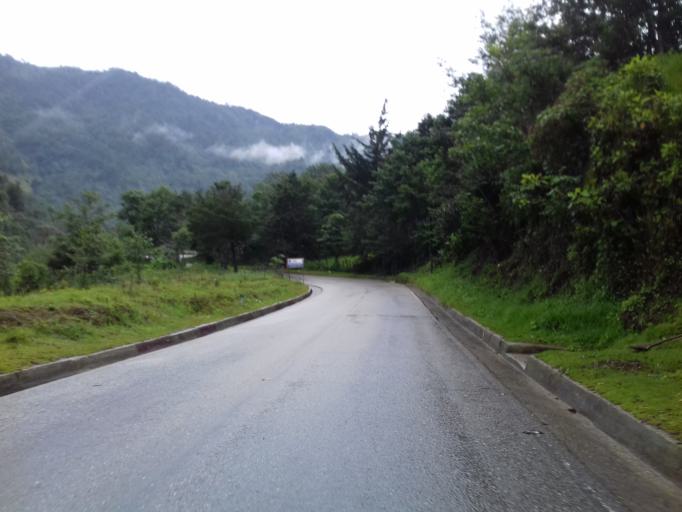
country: GT
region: Quiche
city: Nebaj
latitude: 15.3873
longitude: -91.1154
